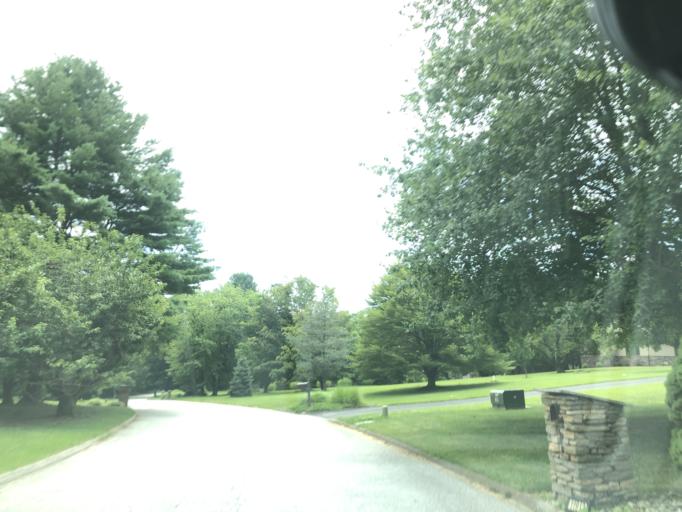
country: US
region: Maryland
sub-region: Baltimore County
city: Garrison
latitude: 39.4516
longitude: -76.7207
